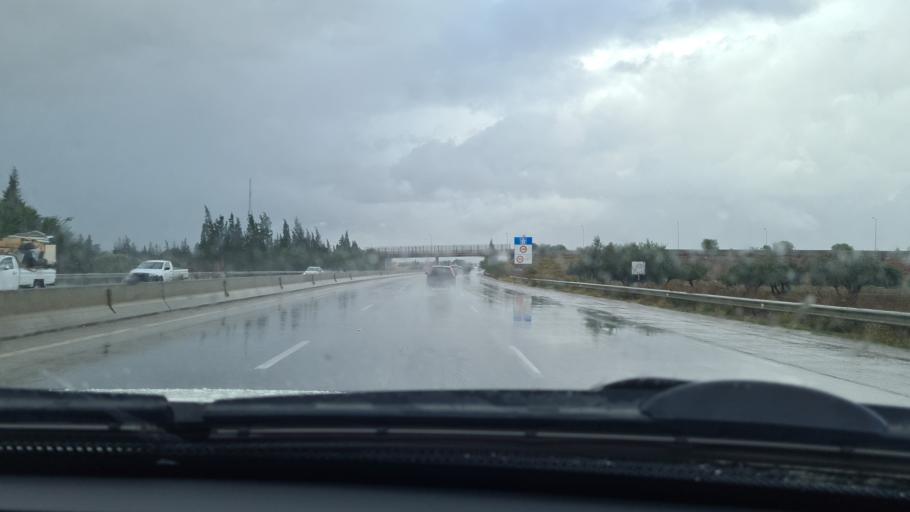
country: TN
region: Tunis
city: La Sebala du Mornag
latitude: 36.7162
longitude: 10.2711
